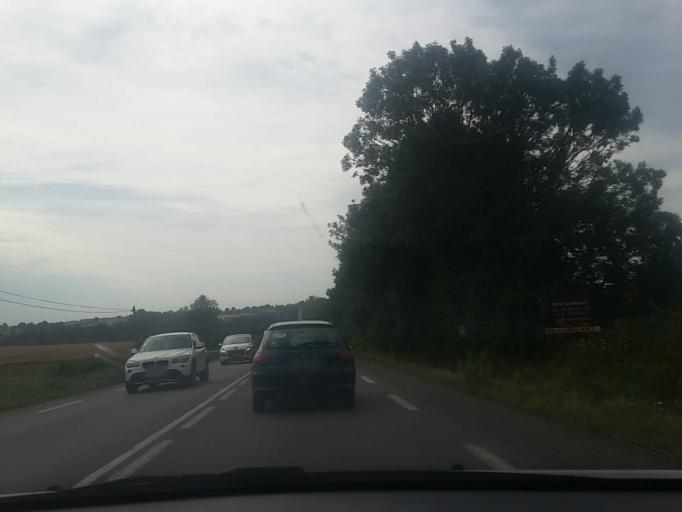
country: FR
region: Pays de la Loire
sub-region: Departement de la Vendee
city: Sainte-Cecile
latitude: 46.7802
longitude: -1.1168
